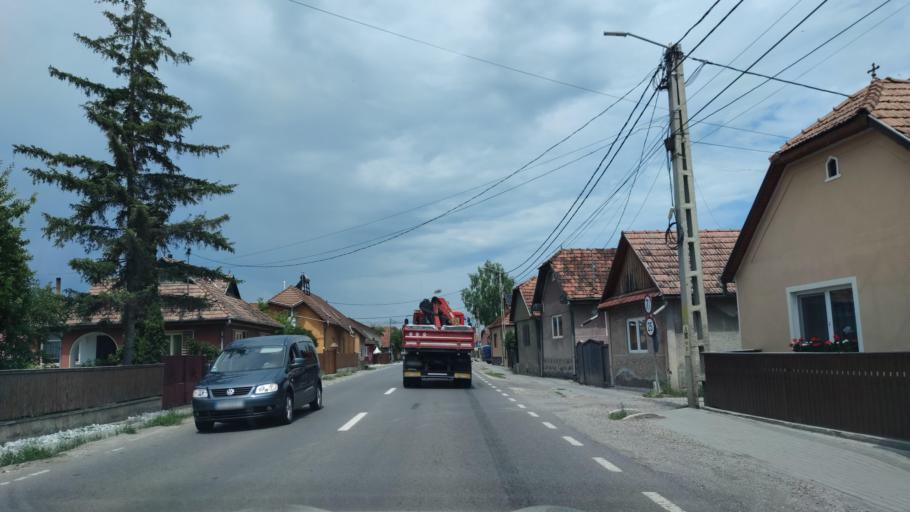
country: RO
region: Harghita
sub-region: Comuna Ciceu
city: Ciceu
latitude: 46.4086
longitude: 25.7842
